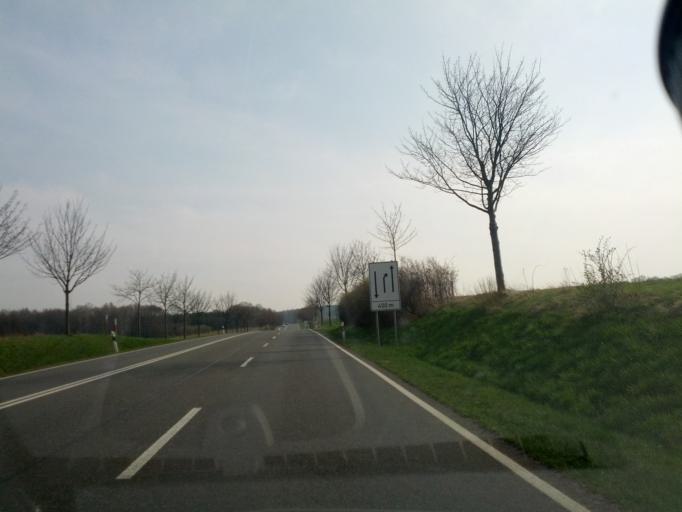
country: DE
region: Saxony
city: Kirchberg
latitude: 50.6409
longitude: 12.5659
